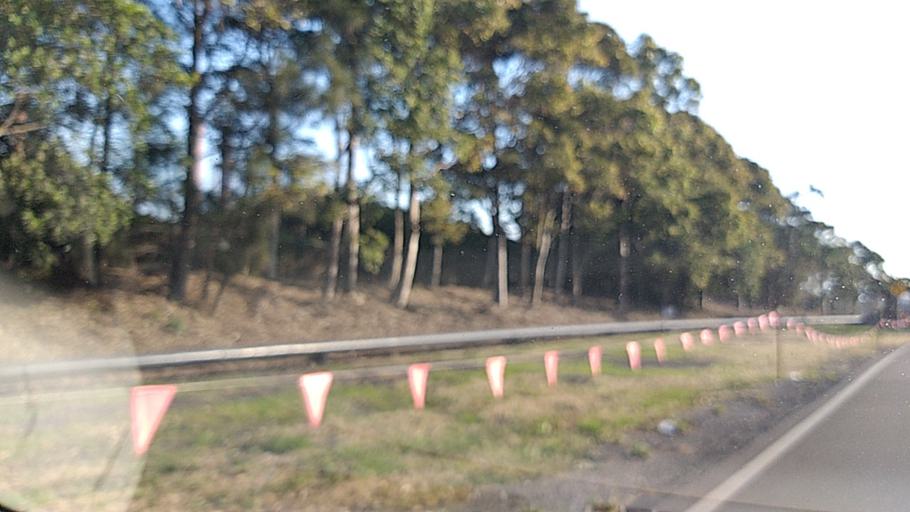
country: AU
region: New South Wales
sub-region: Wollongong
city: Port Kembla
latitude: -34.4663
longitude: 150.8998
